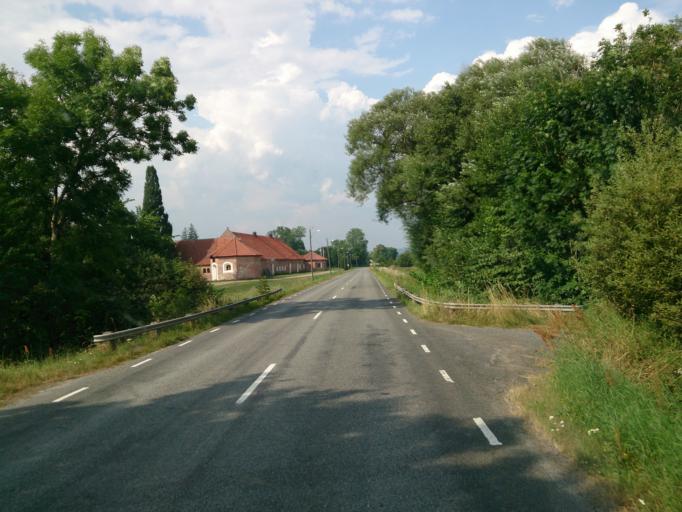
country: SE
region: Skane
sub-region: Kristianstads Kommun
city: Fjalkinge
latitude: 56.0835
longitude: 14.3500
